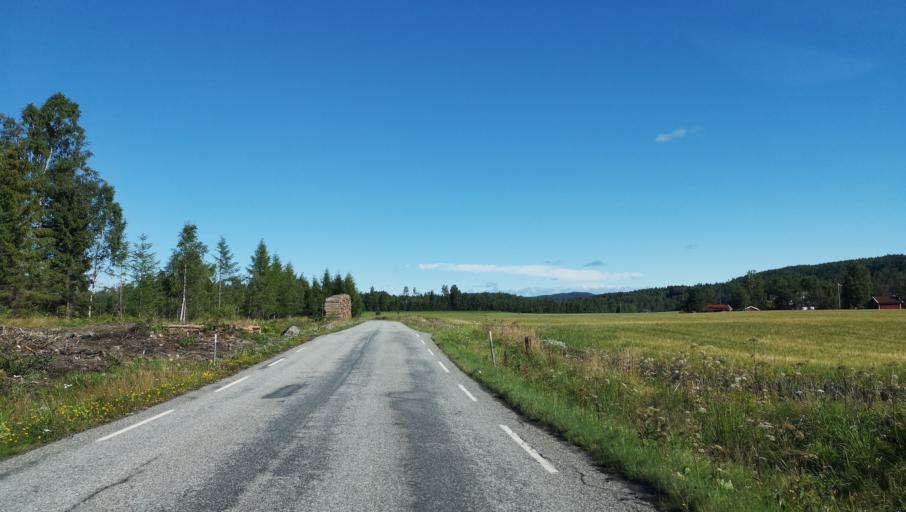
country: NO
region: Ostfold
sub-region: Hobol
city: Knappstad
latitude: 59.6351
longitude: 11.0237
